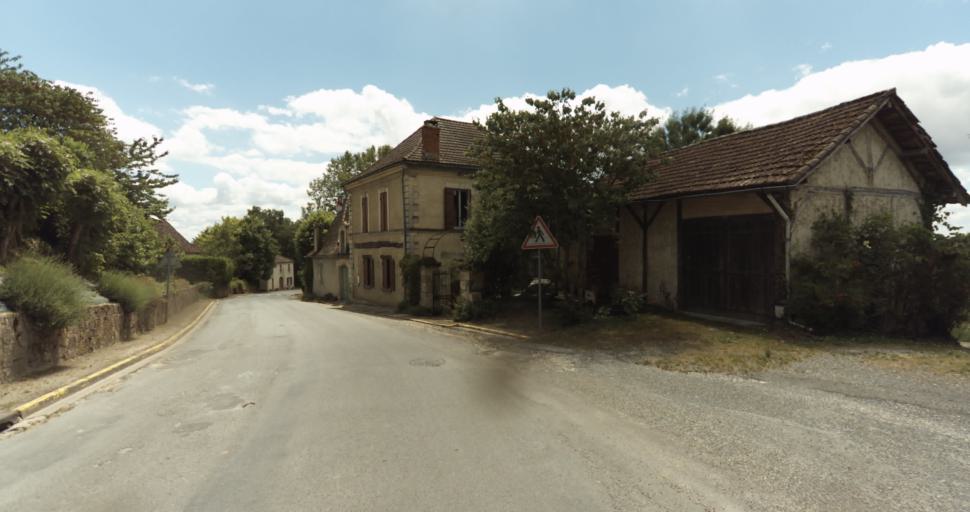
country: FR
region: Aquitaine
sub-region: Departement du Lot-et-Garonne
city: Villereal
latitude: 44.6931
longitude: 0.7514
